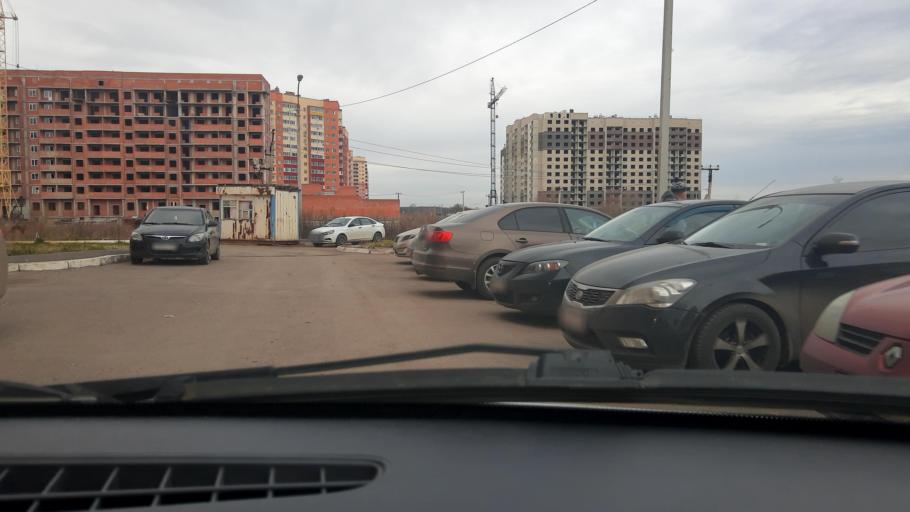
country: RU
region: Bashkortostan
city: Mikhaylovka
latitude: 54.7122
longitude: 55.8478
